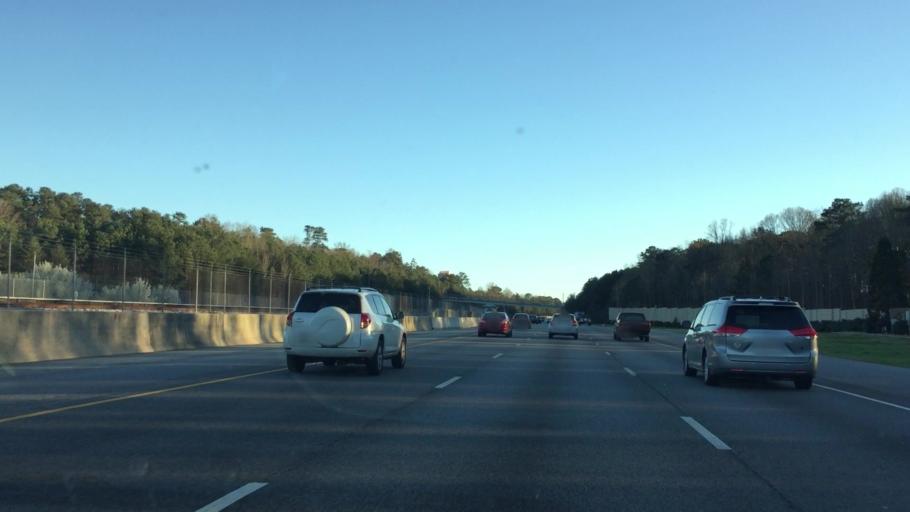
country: US
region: Georgia
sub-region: DeKalb County
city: North Atlanta
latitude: 33.8778
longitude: -84.3651
